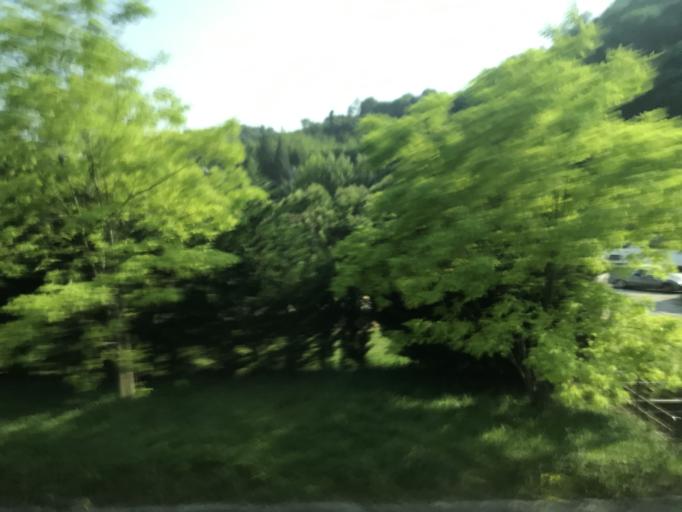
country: ES
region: Basque Country
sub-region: Provincia de Guipuzcoa
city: San Sebastian
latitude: 43.3042
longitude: -1.9635
